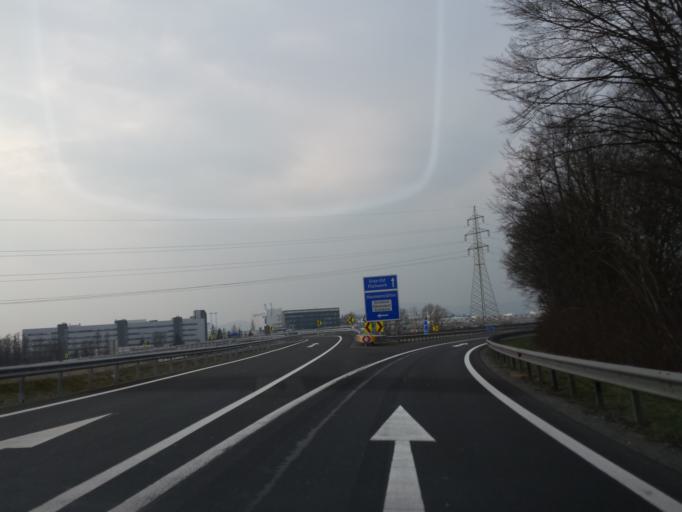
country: AT
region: Styria
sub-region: Politischer Bezirk Graz-Umgebung
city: Grambach
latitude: 47.0208
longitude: 15.4885
